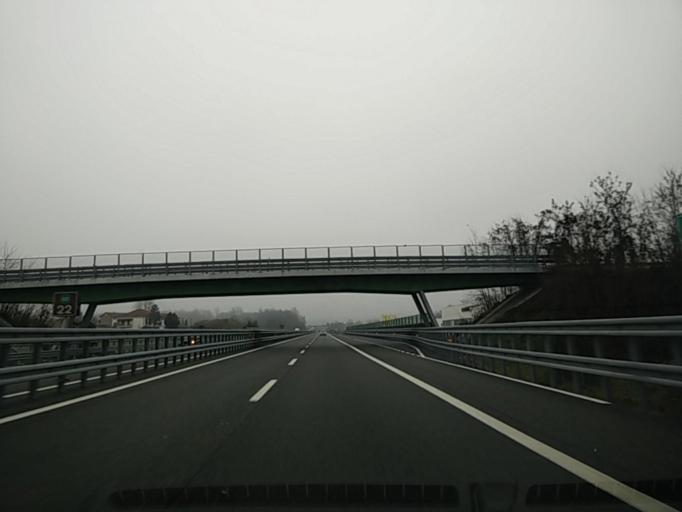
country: IT
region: Piedmont
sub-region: Provincia di Asti
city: Cantarana
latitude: 44.9086
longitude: 8.0499
